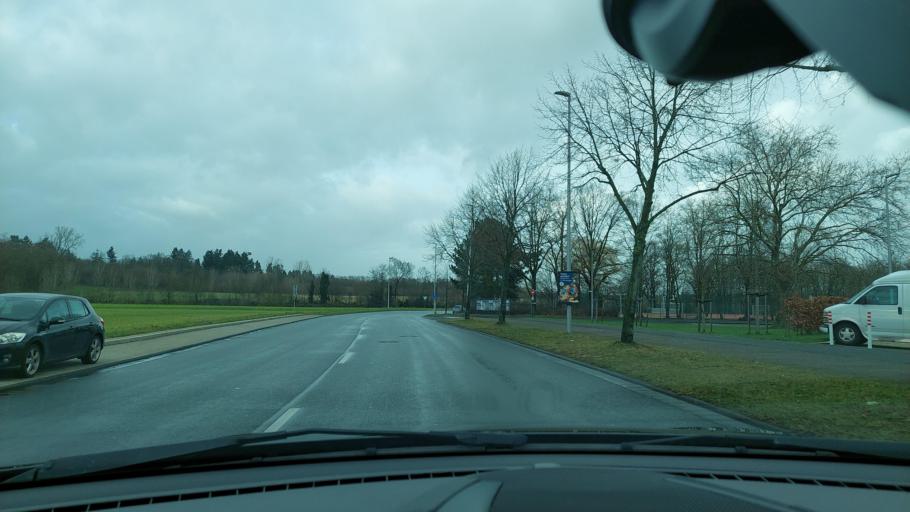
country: DE
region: North Rhine-Westphalia
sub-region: Regierungsbezirk Dusseldorf
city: Dormagen
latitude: 51.0749
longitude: 6.8077
